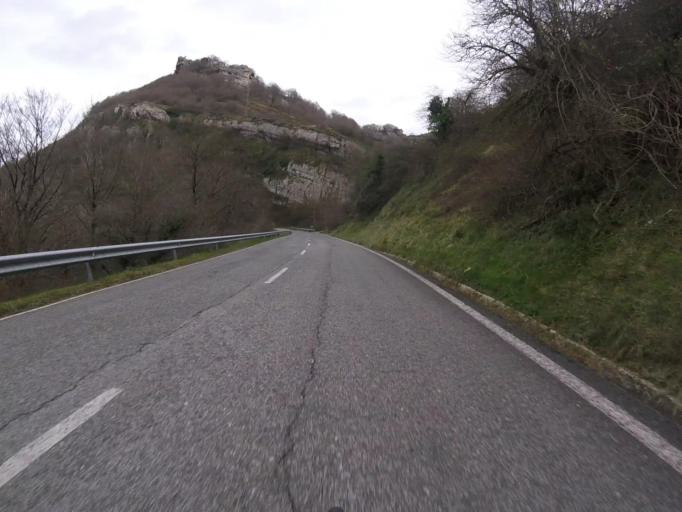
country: ES
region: Navarre
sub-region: Provincia de Navarra
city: Olazagutia
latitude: 42.8609
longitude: -2.1864
